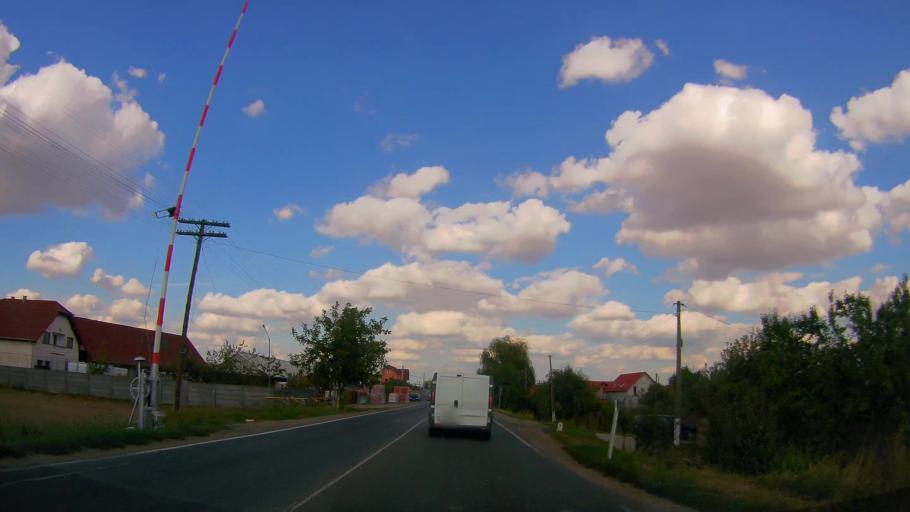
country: RO
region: Satu Mare
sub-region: Comuna Botiz
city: Botiz
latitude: 47.8231
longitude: 22.9420
